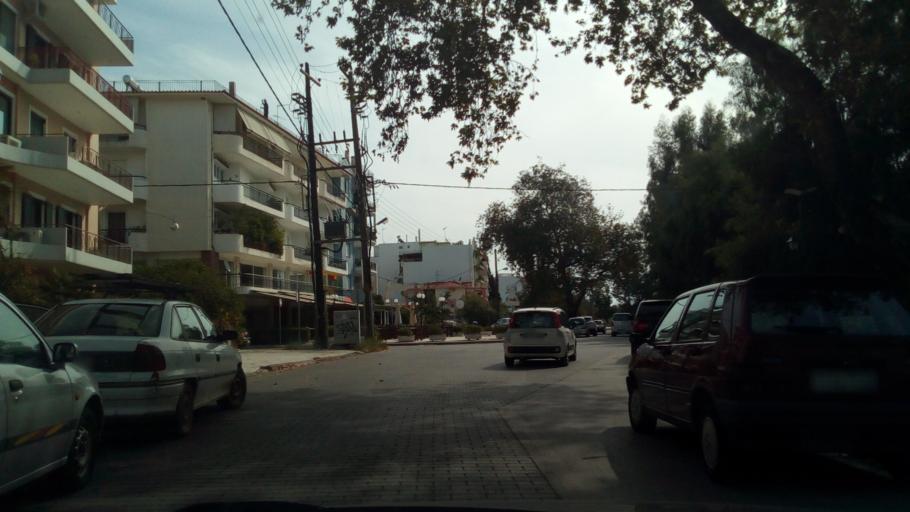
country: GR
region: West Greece
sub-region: Nomos Aitolias kai Akarnanias
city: Nafpaktos
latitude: 38.3904
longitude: 21.8402
